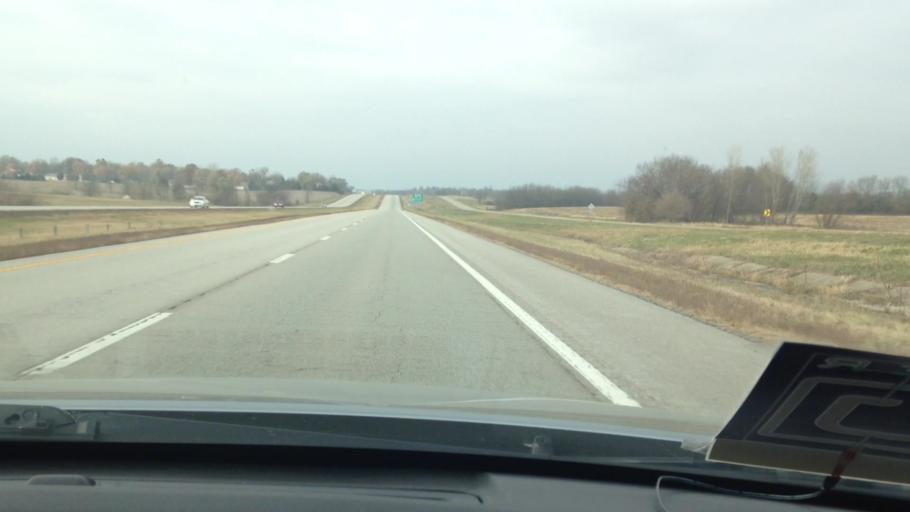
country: US
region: Missouri
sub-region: Cass County
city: Garden City
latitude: 38.5559
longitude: -94.1794
